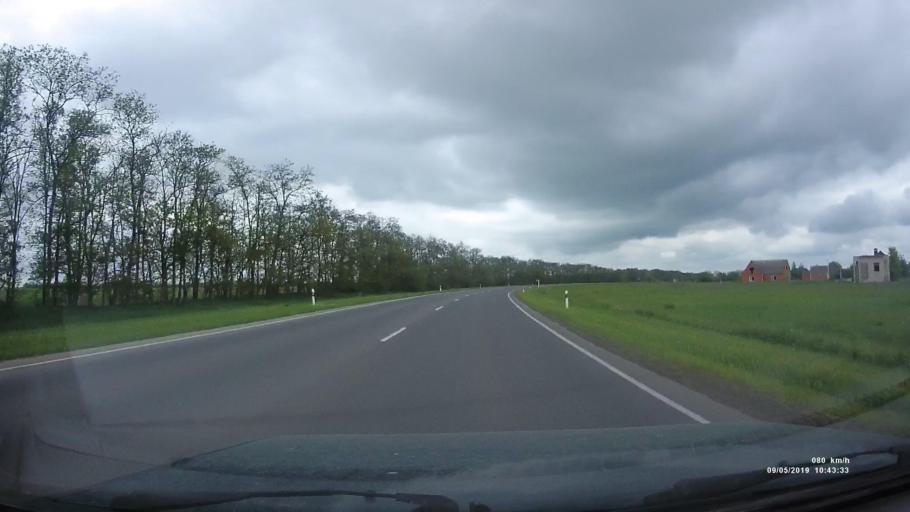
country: RU
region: Rostov
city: Peshkovo
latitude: 47.0070
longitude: 39.4022
